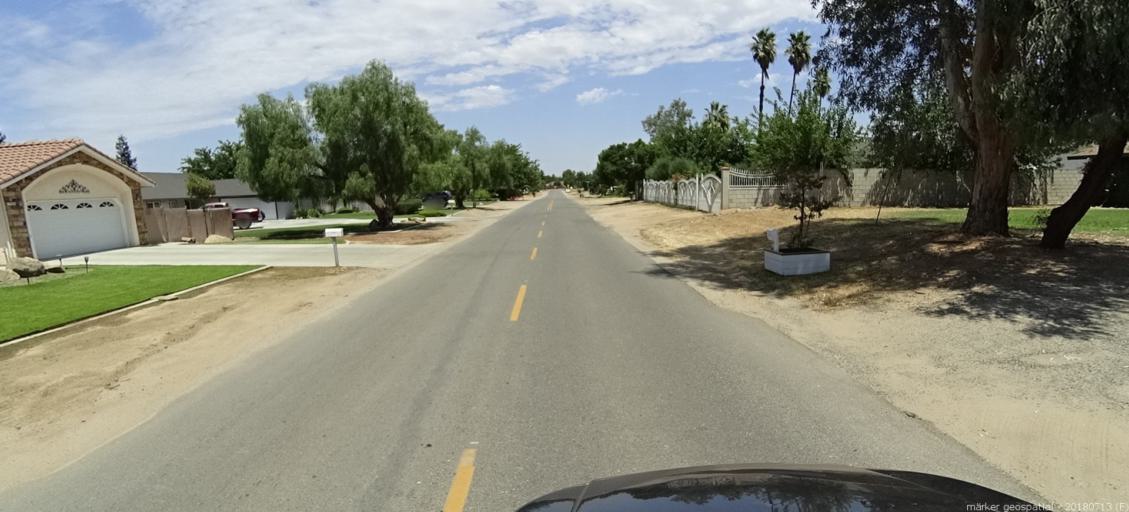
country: US
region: California
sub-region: Madera County
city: Madera Acres
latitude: 36.9982
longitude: -120.0821
